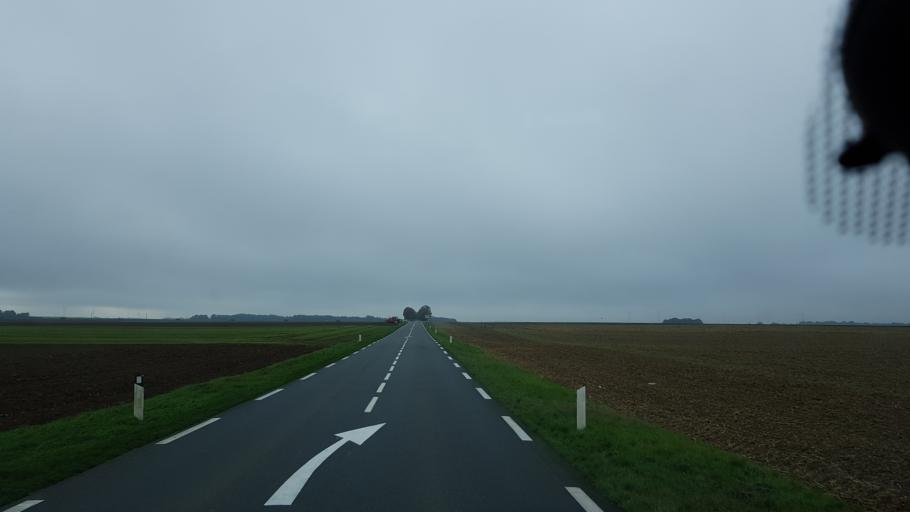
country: FR
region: Ile-de-France
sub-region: Departement de l'Essonne
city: Pussay
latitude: 48.4184
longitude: 1.9651
